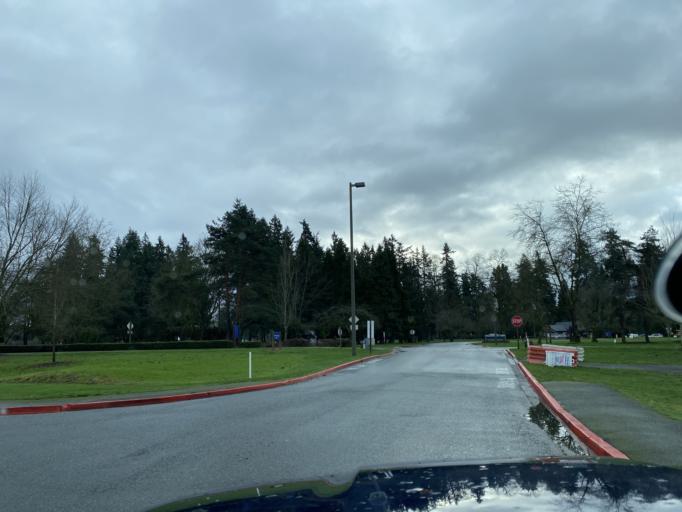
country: US
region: Washington
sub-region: King County
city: Redmond
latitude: 47.6644
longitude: -122.1216
